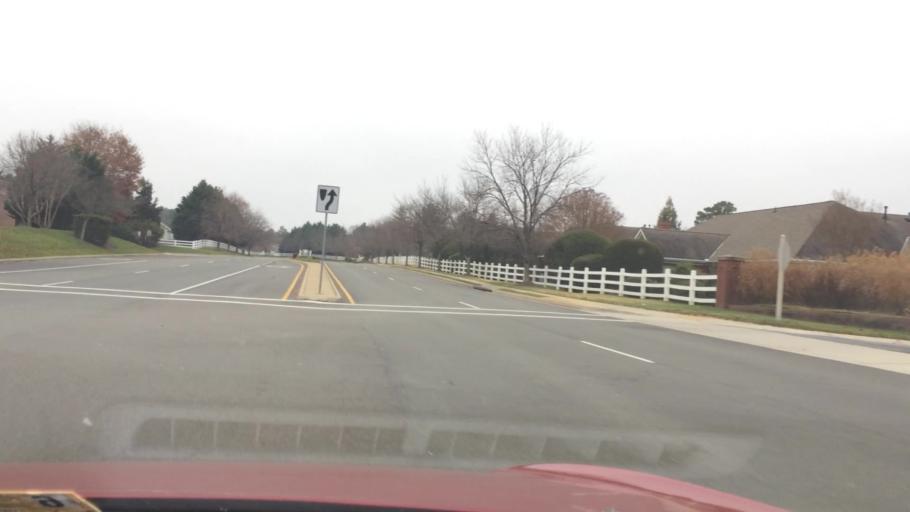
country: US
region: Virginia
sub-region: Henrico County
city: Glen Allen
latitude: 37.6712
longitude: -77.4648
